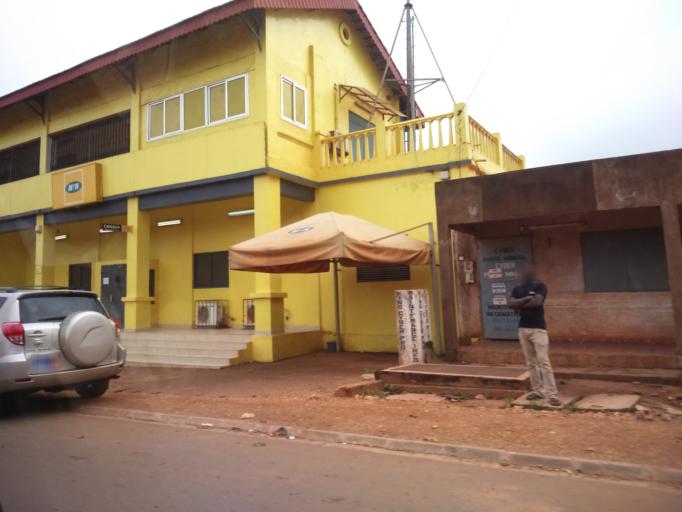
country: CI
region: Moyen-Comoe
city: Abengourou
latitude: 6.7310
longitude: -3.4870
